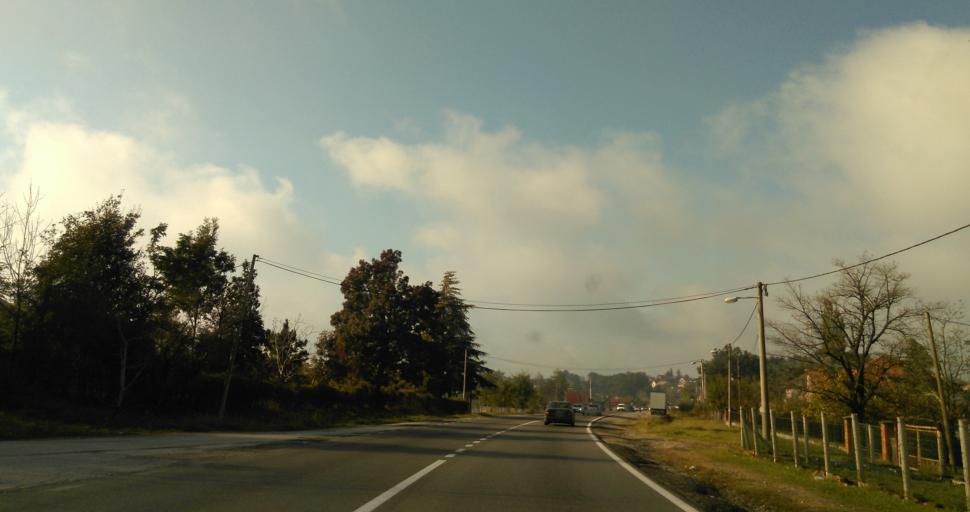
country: RS
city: Vranic
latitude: 44.6094
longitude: 20.3590
